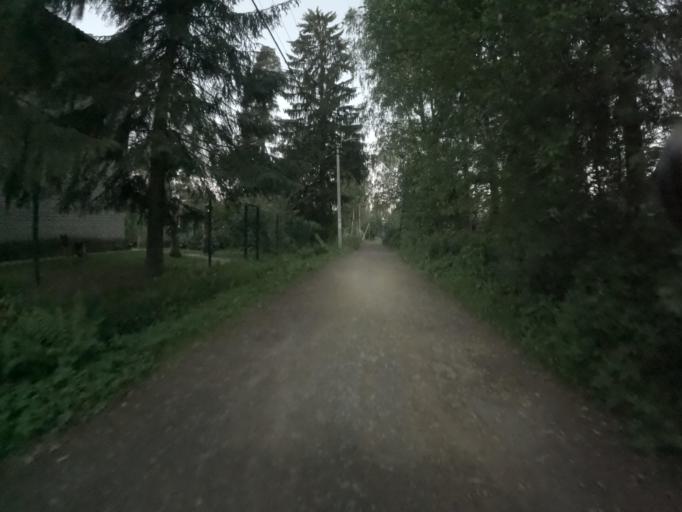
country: RU
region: Leningrad
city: Vsevolozhsk
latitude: 60.0170
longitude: 30.6154
